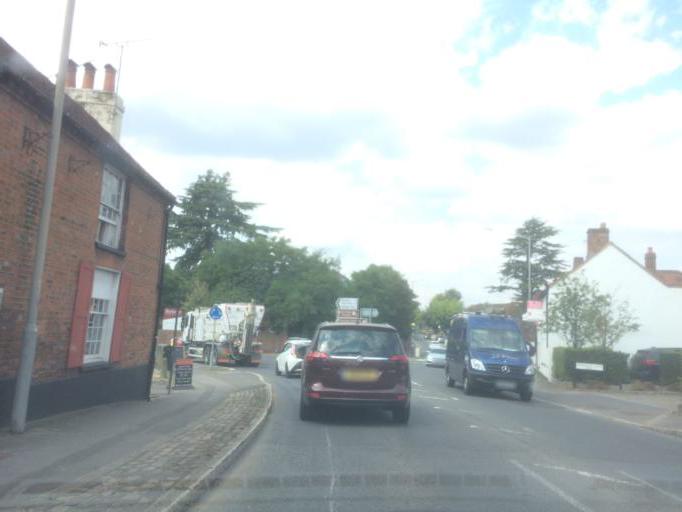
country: GB
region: England
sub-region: Buckinghamshire
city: Farnham Royal
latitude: 51.5368
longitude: -0.6174
